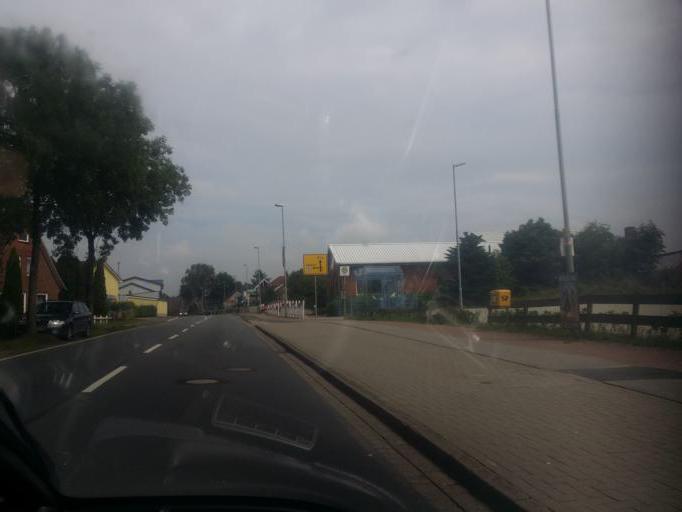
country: DE
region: Schleswig-Holstein
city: Sankt Michaelisdonn
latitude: 53.9941
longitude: 9.1189
